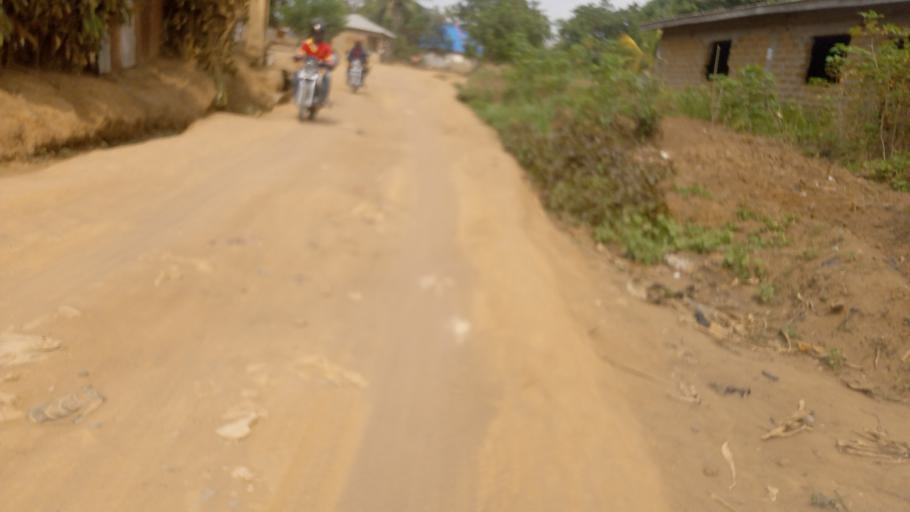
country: SL
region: Western Area
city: Waterloo
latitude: 8.3228
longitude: -13.0571
